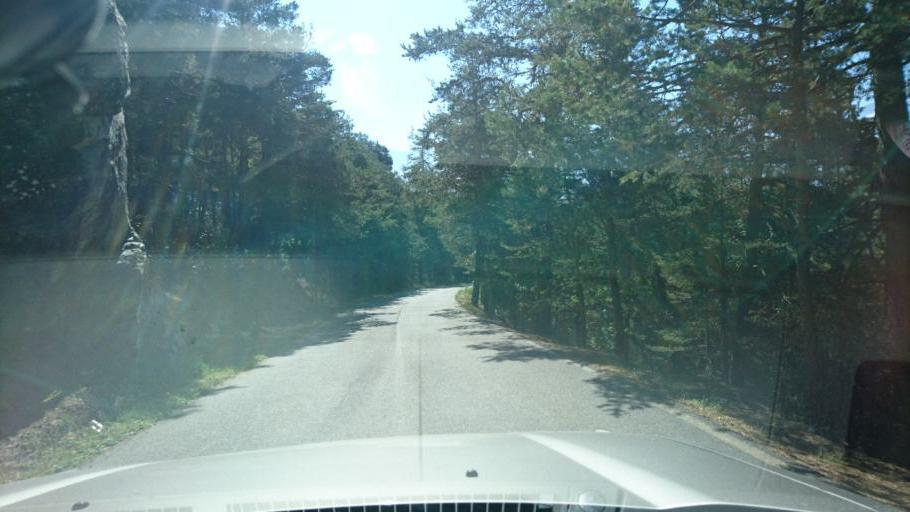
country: IT
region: Aosta Valley
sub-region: Valle d'Aosta
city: Ville Sur Sarre
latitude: 45.7338
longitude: 7.2454
